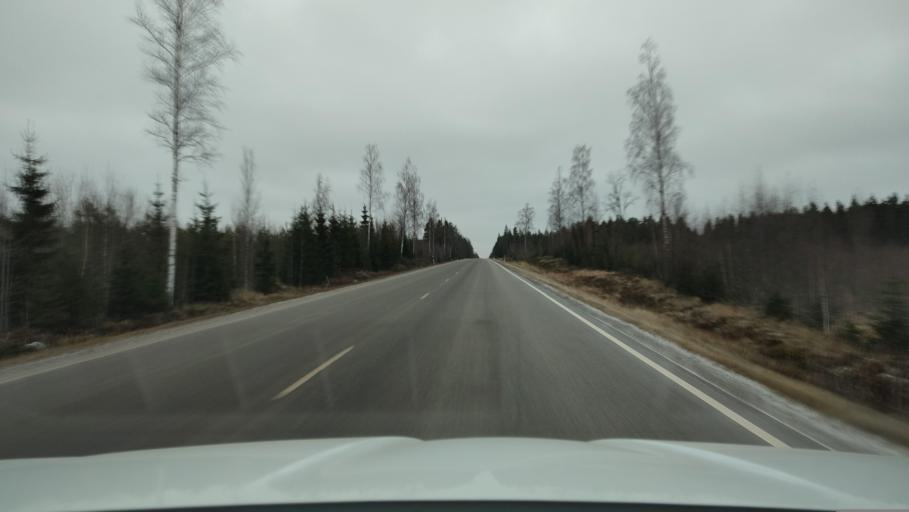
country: FI
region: Ostrobothnia
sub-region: Sydosterbotten
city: Naerpes
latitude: 62.4888
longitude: 21.4432
